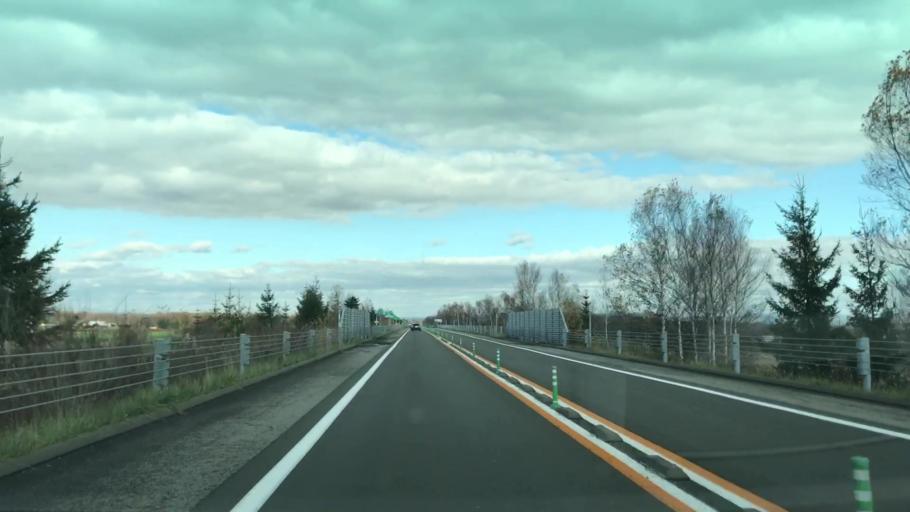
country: JP
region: Hokkaido
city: Chitose
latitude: 42.8670
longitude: 141.6105
